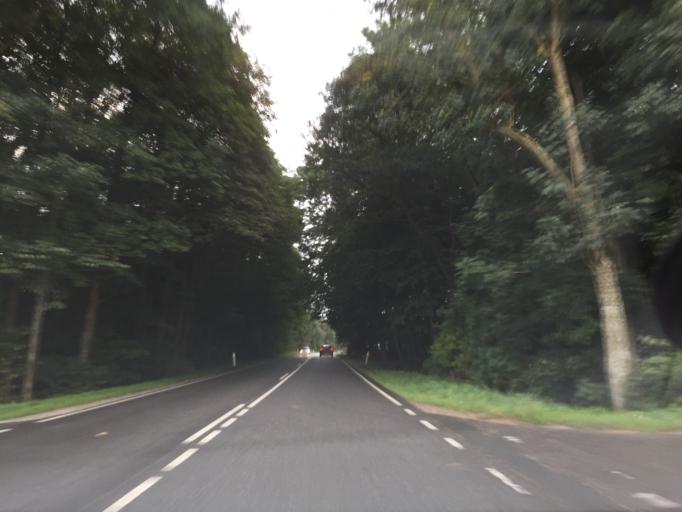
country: DK
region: Central Jutland
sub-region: Skanderborg Kommune
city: Skanderborg
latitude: 56.0816
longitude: 9.8989
